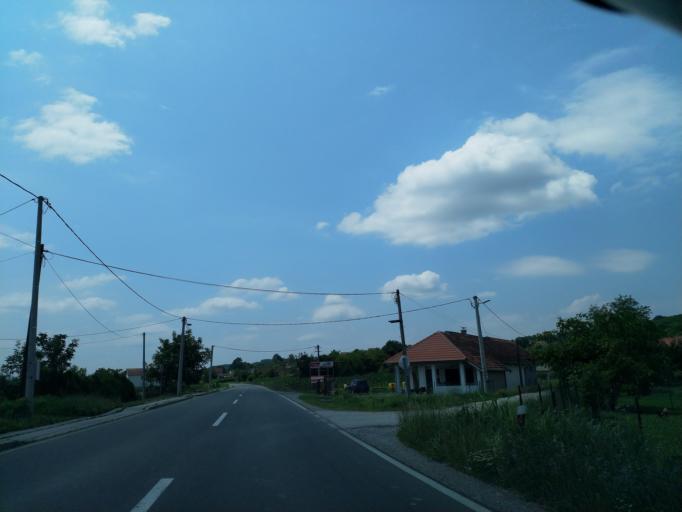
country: RS
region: Central Serbia
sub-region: Rasinski Okrug
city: Krusevac
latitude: 43.4991
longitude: 21.2921
